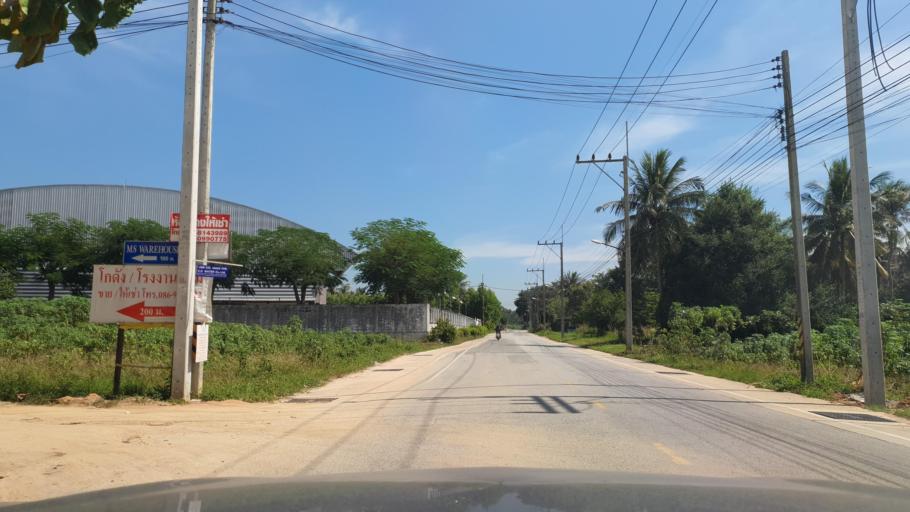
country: TH
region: Chon Buri
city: Bang Lamung
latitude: 12.9840
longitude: 100.9750
